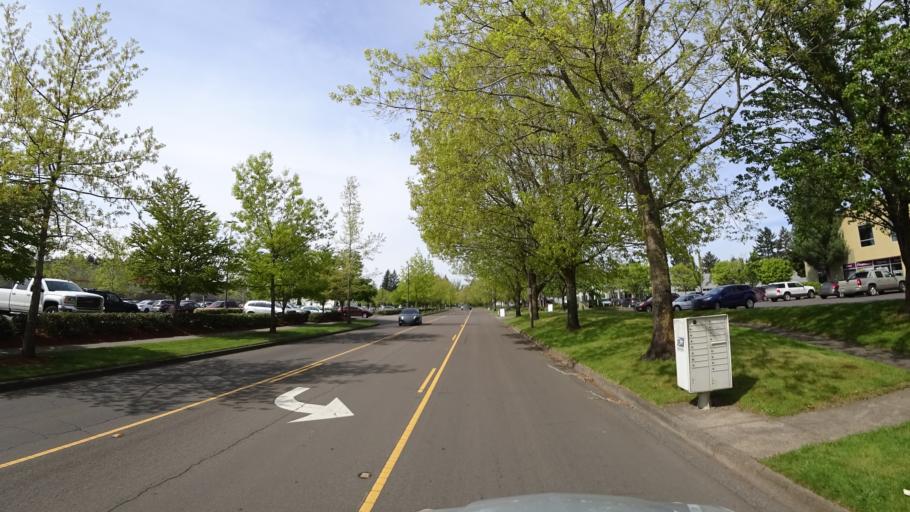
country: US
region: Oregon
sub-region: Washington County
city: Hillsboro
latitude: 45.5355
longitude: -122.9337
